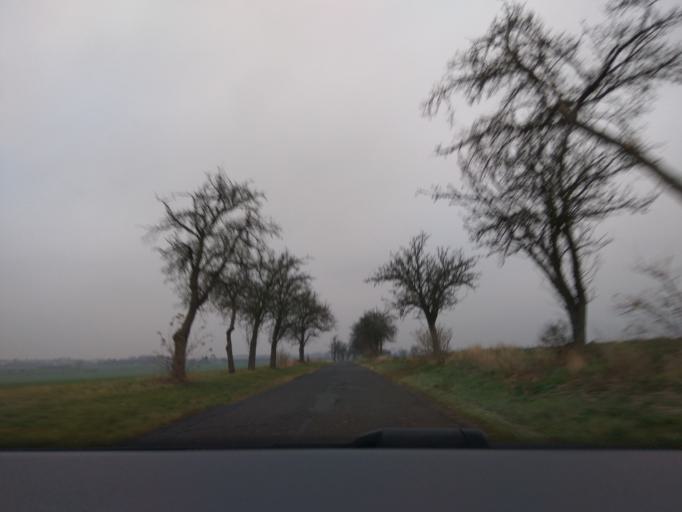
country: CZ
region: Praha
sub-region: Praha 19
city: Kbely
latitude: 50.1541
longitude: 14.5568
